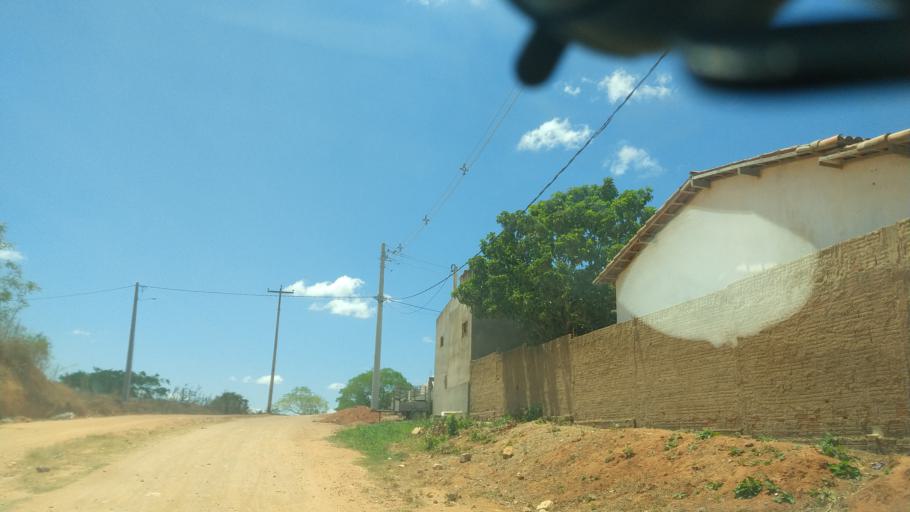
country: BR
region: Rio Grande do Norte
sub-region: Cerro Cora
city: Cerro Cora
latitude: -6.0341
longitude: -36.3450
